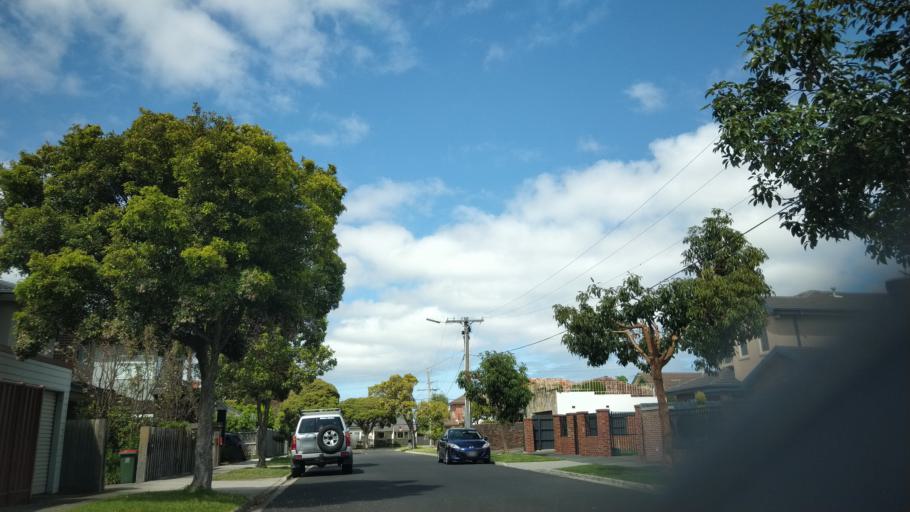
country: AU
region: Victoria
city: Murrumbeena
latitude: -37.8988
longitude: 145.0569
